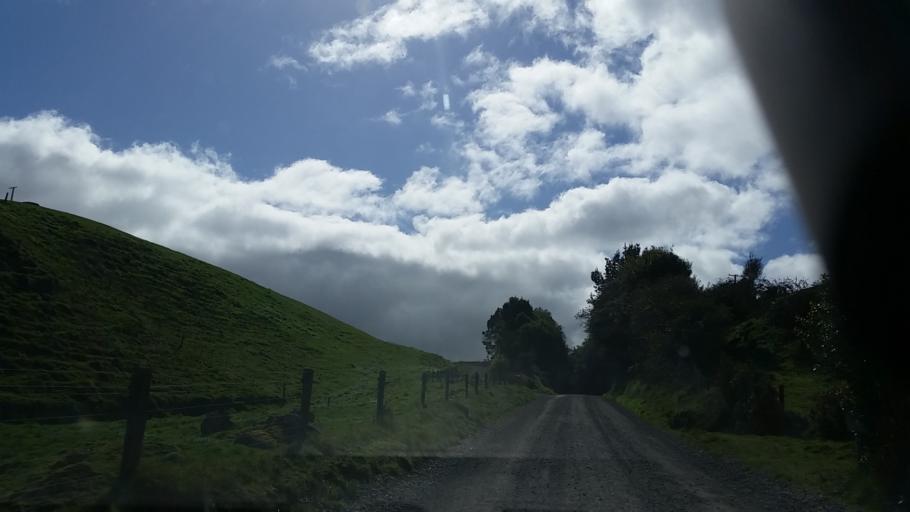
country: NZ
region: Bay of Plenty
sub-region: Rotorua District
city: Rotorua
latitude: -38.3728
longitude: 176.1216
